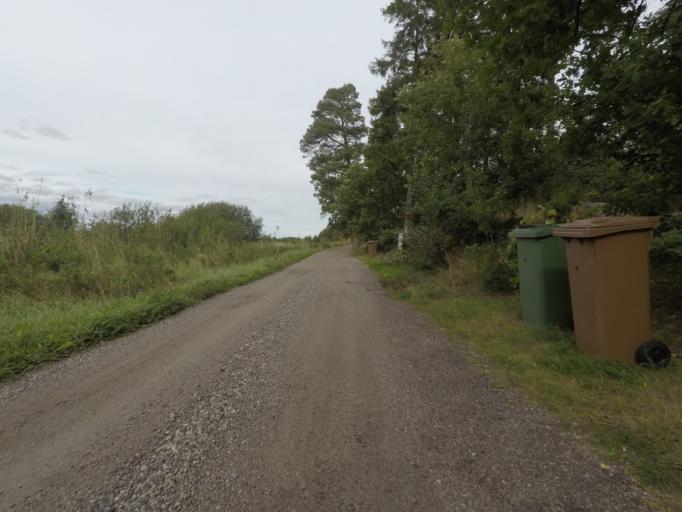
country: SE
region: Vaestmanland
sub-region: Kungsors Kommun
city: Kungsoer
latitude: 59.4613
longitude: 16.0709
